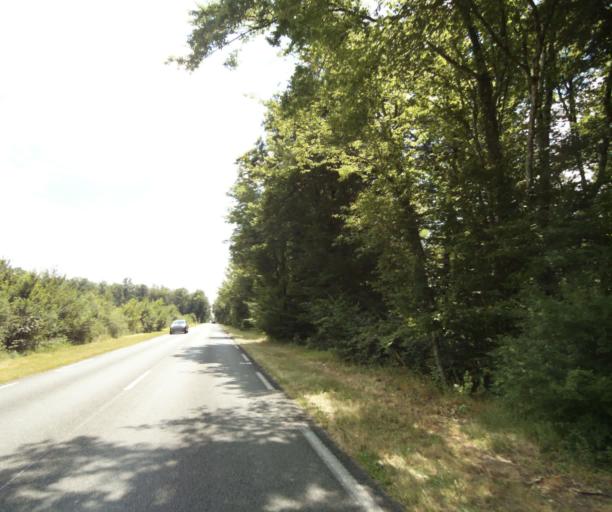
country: FR
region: Ile-de-France
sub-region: Departement de Seine-et-Marne
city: Bois-le-Roi
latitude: 48.4537
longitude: 2.7060
